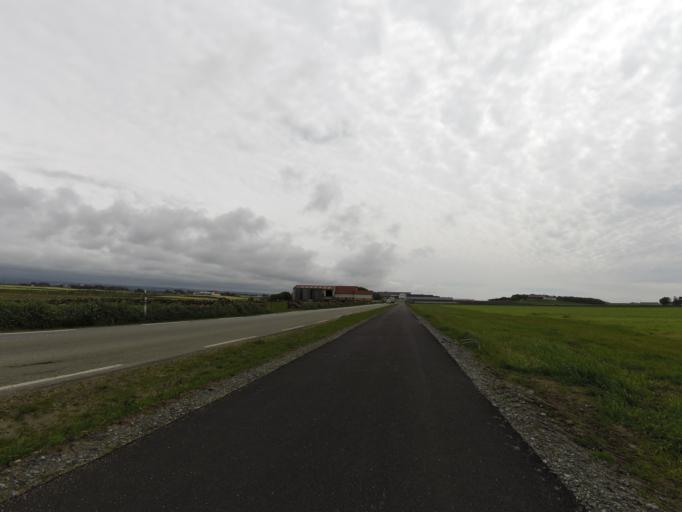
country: NO
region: Rogaland
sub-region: Ha
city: Naerbo
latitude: 58.6849
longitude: 5.5632
